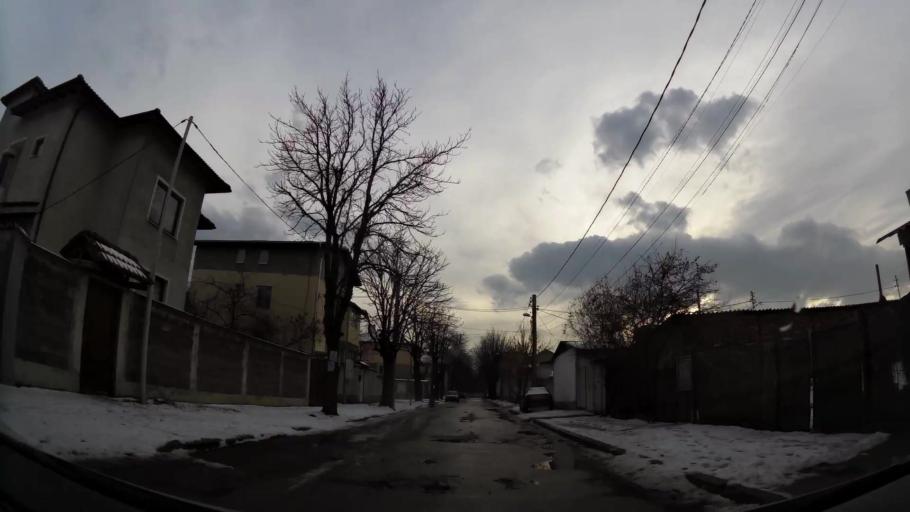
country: BG
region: Sofia-Capital
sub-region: Stolichna Obshtina
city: Sofia
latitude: 42.7199
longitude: 23.3376
